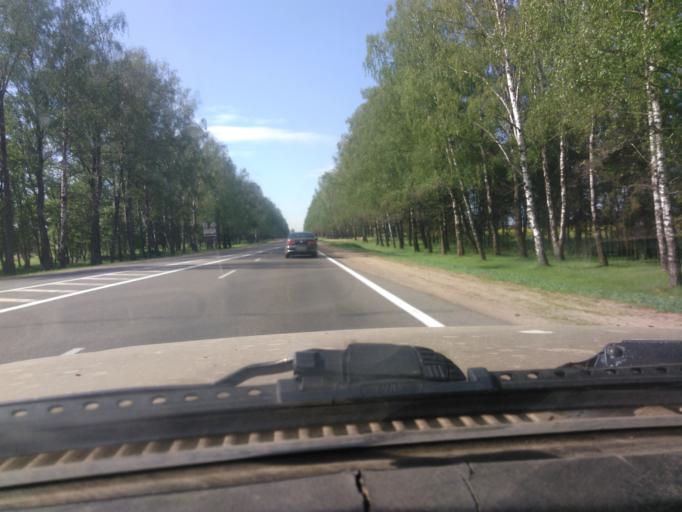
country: BY
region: Mogilev
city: Buynichy
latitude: 53.8479
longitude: 30.2518
